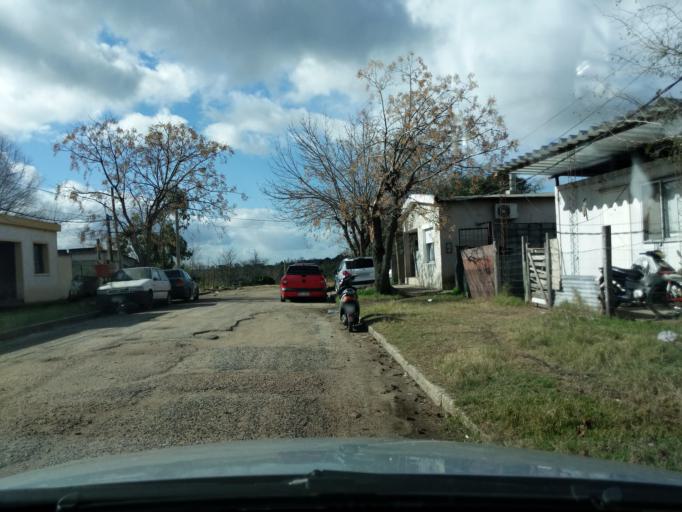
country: UY
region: Florida
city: Florida
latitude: -34.0948
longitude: -56.2070
